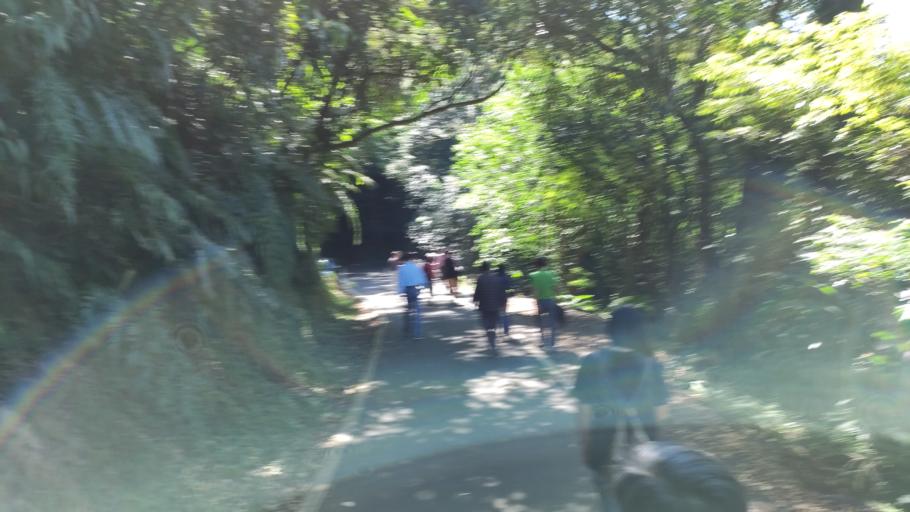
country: TW
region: Taiwan
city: Daxi
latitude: 24.8381
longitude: 121.3063
